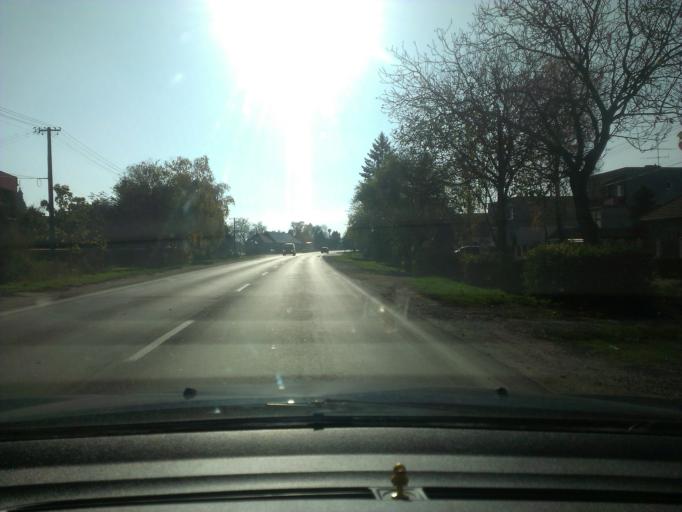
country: SK
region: Nitriansky
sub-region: Okres Nitra
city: Nitra
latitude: 48.2132
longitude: 18.1464
